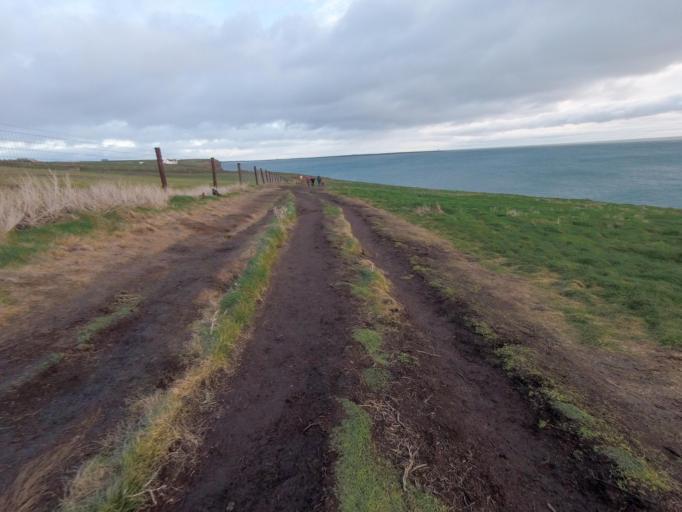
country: IE
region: Munster
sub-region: Waterford
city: Dunmore East
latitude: 52.1393
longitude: -7.0102
